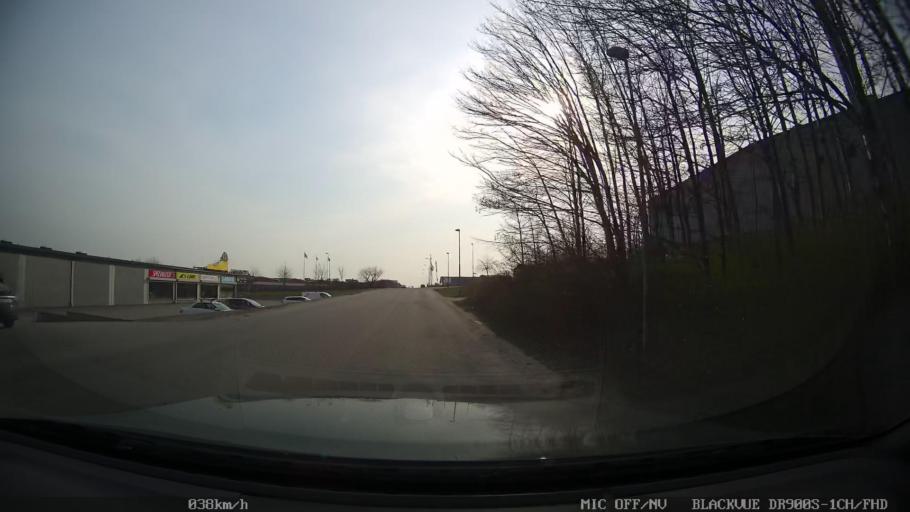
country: SE
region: Skane
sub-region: Ystads Kommun
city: Ystad
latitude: 55.4481
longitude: 13.8459
